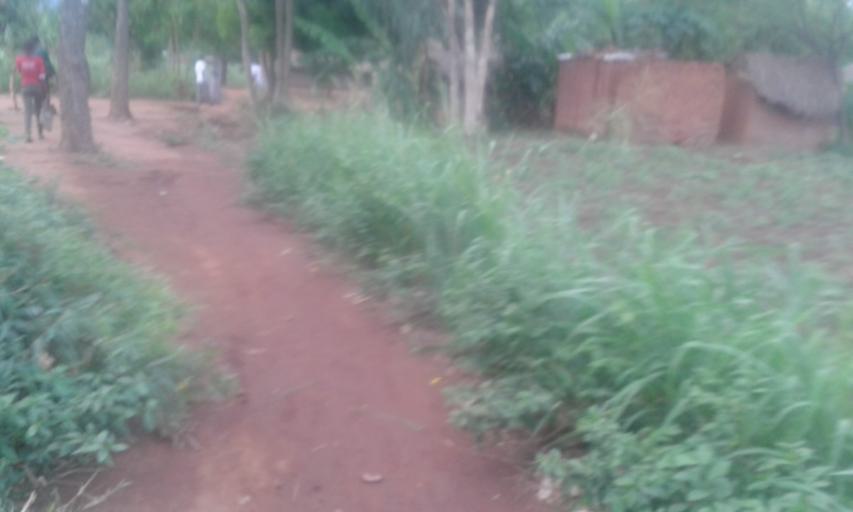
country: UG
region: Northern Region
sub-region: Gulu District
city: Gulu
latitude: 2.7924
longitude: 32.3226
